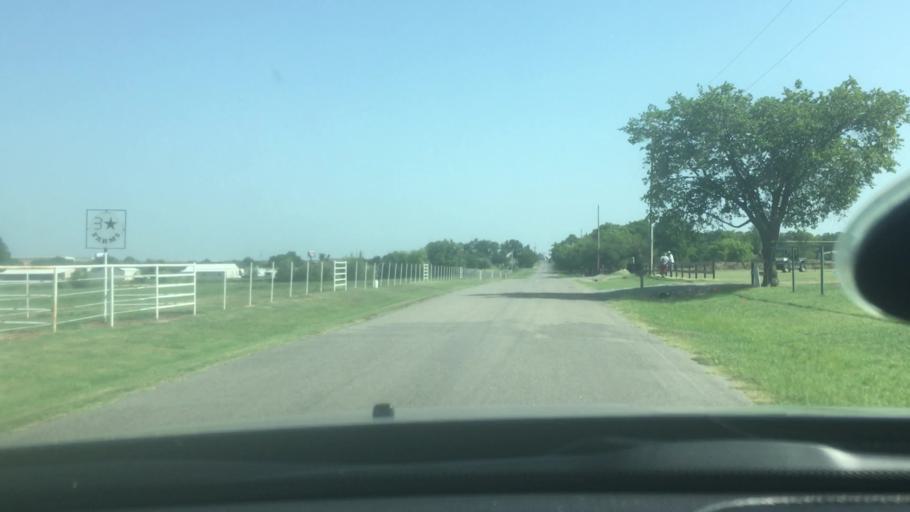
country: US
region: Oklahoma
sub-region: Bryan County
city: Calera
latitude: 33.9915
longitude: -96.4656
